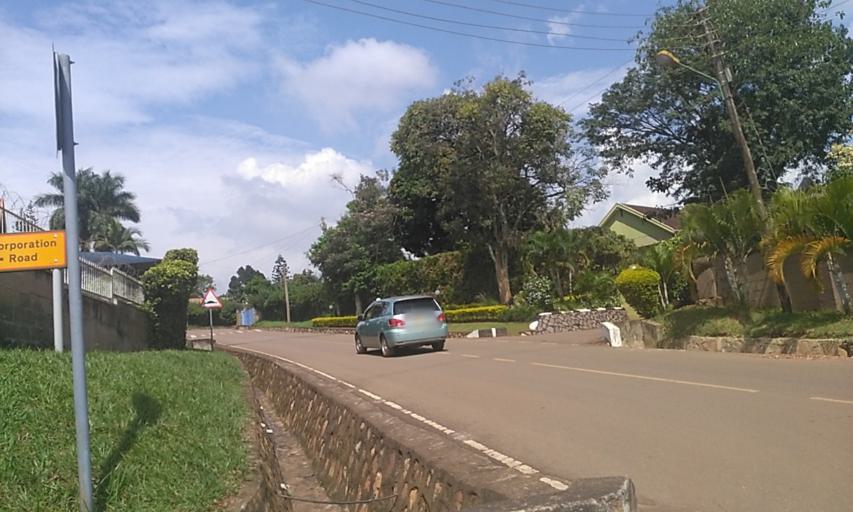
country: UG
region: Central Region
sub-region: Wakiso District
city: Kireka
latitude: 0.3543
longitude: 32.6204
